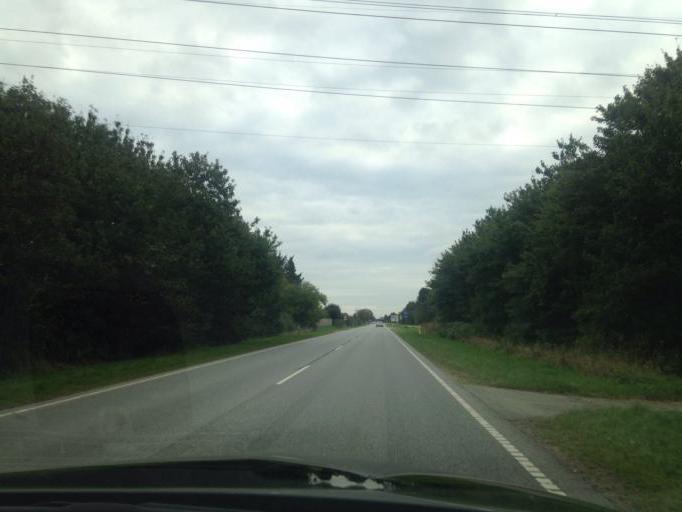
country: DK
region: South Denmark
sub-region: Haderslev Kommune
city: Vojens
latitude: 55.2538
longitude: 9.3487
